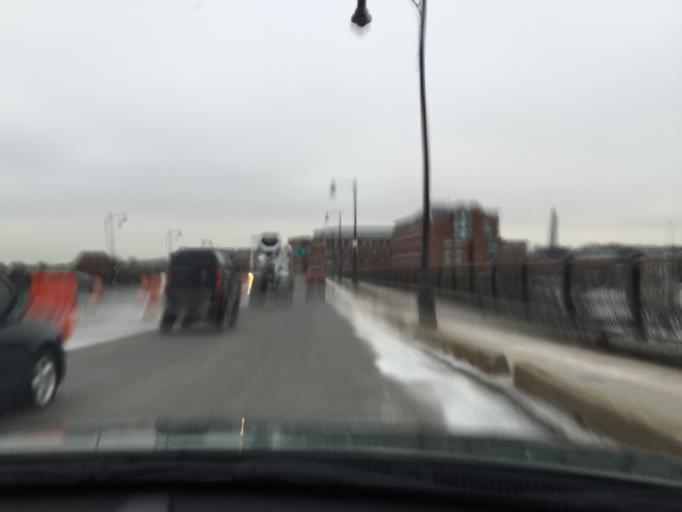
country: US
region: Massachusetts
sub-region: Suffolk County
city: Boston
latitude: 42.3690
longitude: -71.0599
